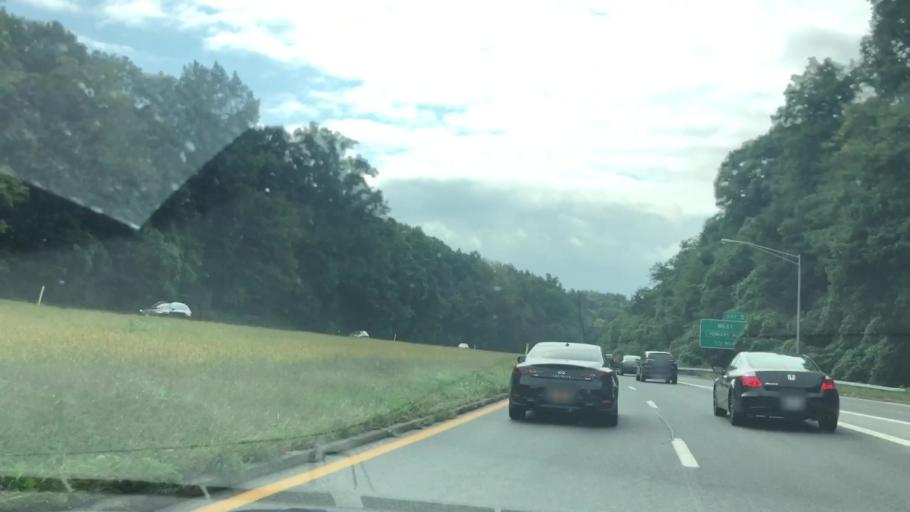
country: US
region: New York
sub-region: Westchester County
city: Yonkers
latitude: 40.9422
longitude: -73.8757
